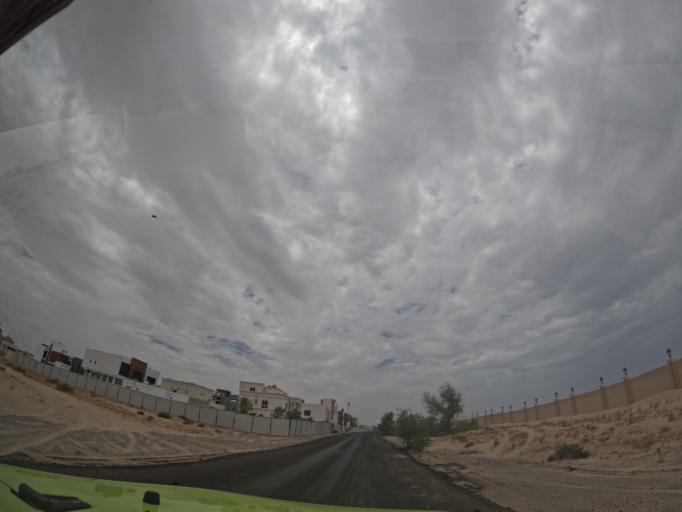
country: AE
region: Ash Shariqah
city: Sharjah
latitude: 25.1529
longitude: 55.3729
